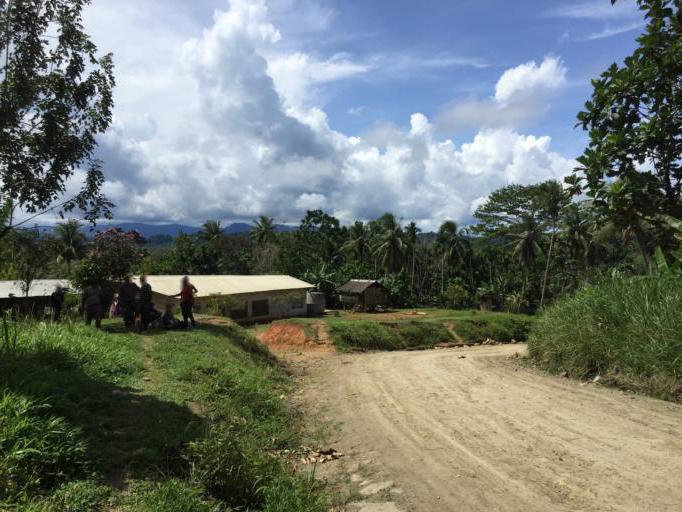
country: PG
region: Gulf
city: Kerema
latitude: -7.9783
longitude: 145.7943
